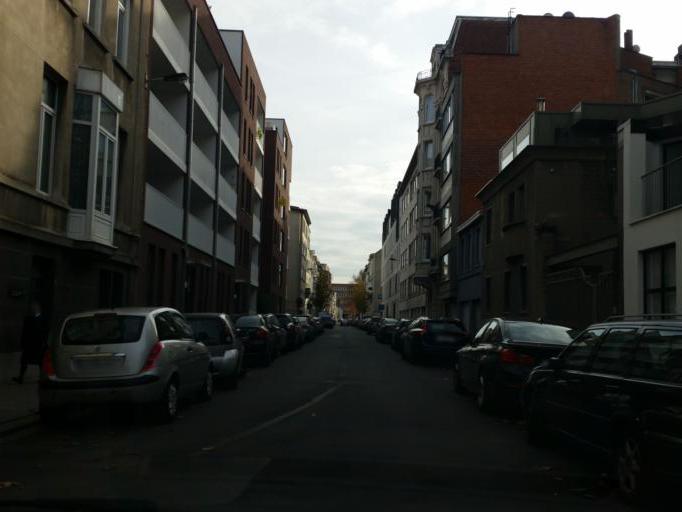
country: BE
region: Flanders
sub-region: Provincie Antwerpen
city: Antwerpen
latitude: 51.2032
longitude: 4.4148
